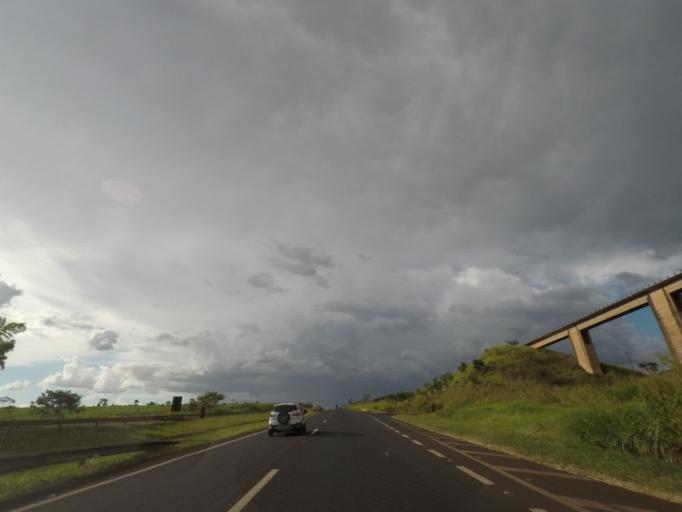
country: BR
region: Sao Paulo
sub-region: Jardinopolis
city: Jardinopolis
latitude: -21.0075
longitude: -47.8467
